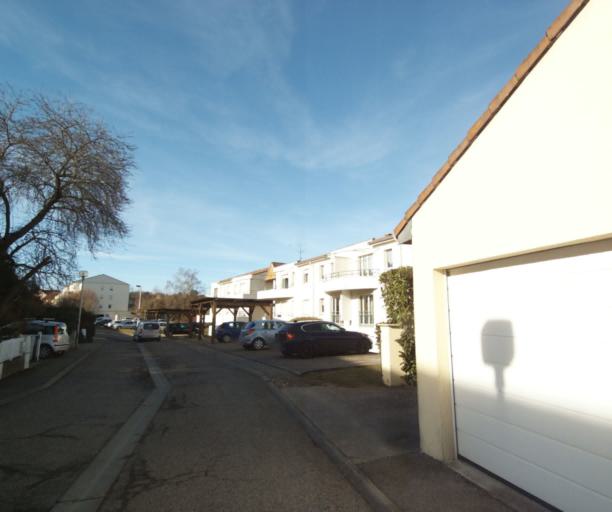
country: FR
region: Lorraine
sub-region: Departement de Meurthe-et-Moselle
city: Villers-les-Nancy
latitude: 48.6513
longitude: 6.1580
